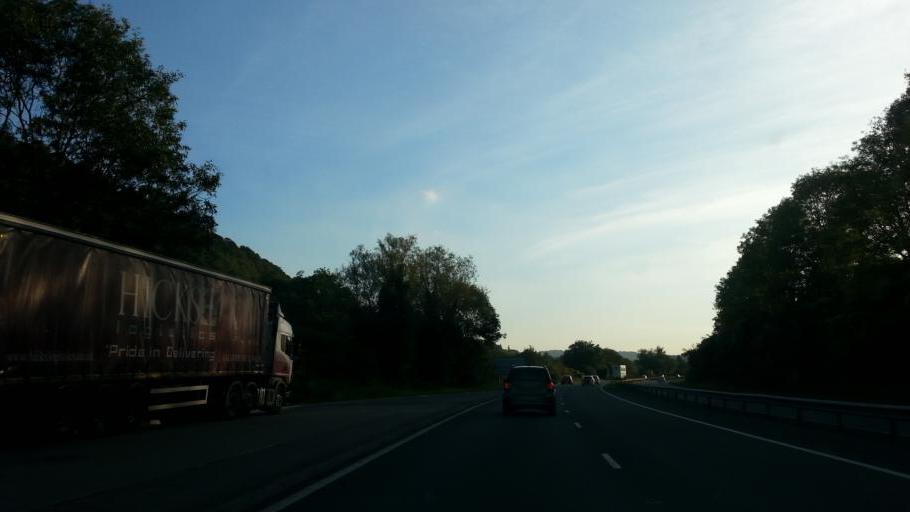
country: GB
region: Wales
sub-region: Monmouthshire
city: Monmouth
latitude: 51.8235
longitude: -2.6903
